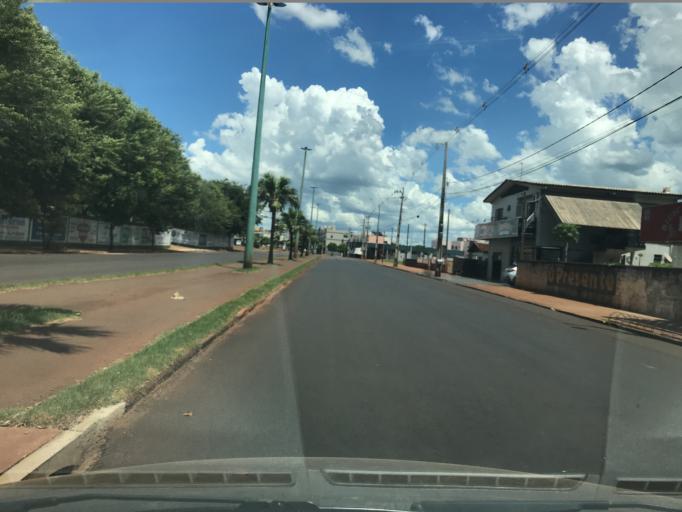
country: BR
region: Parana
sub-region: Palotina
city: Palotina
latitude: -24.2764
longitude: -53.8417
